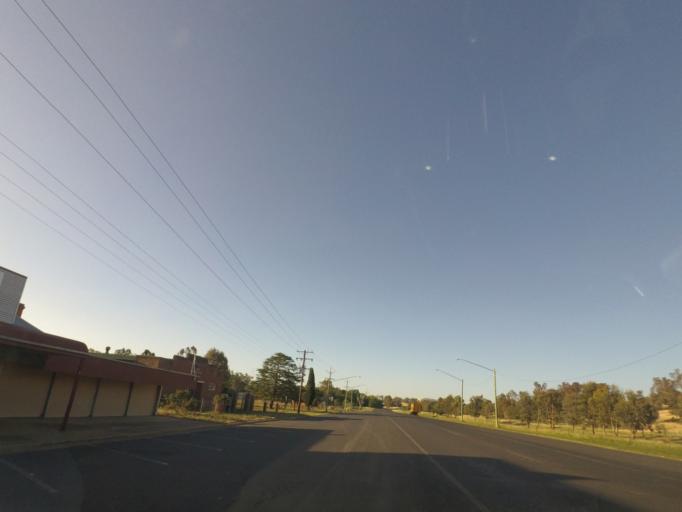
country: AU
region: New South Wales
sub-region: Gundagai
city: Gundagai
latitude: -34.9290
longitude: 148.1663
